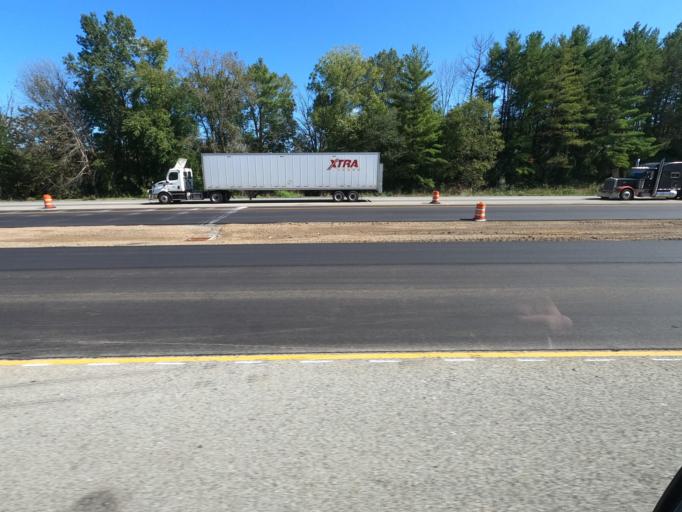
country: US
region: Illinois
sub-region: Franklin County
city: West Frankfort
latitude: 37.8782
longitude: -88.9419
